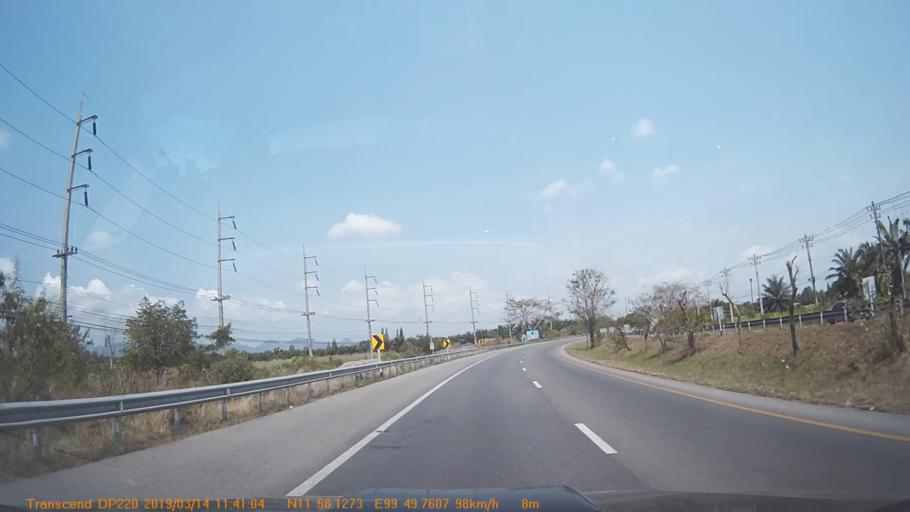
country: TH
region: Prachuap Khiri Khan
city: Kui Buri
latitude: 11.9690
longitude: 99.8292
